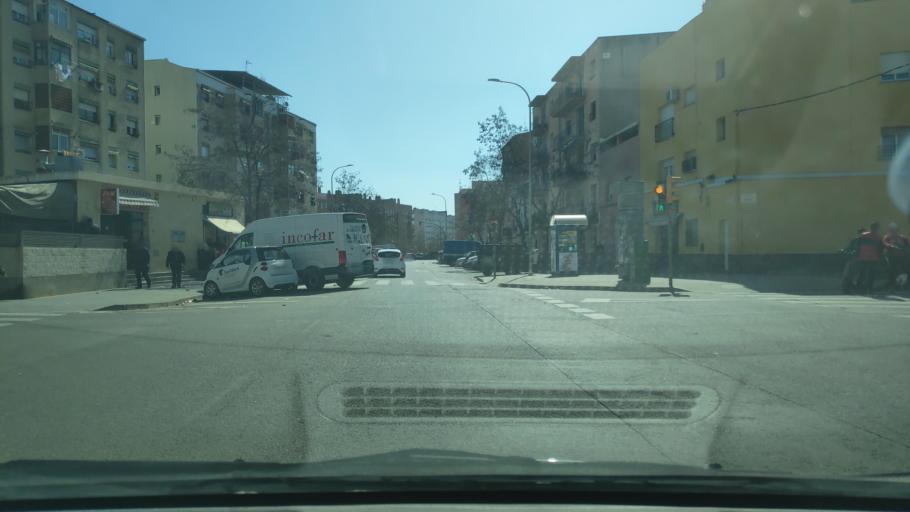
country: ES
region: Catalonia
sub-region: Provincia de Barcelona
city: Sabadell
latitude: 41.5503
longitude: 2.1272
